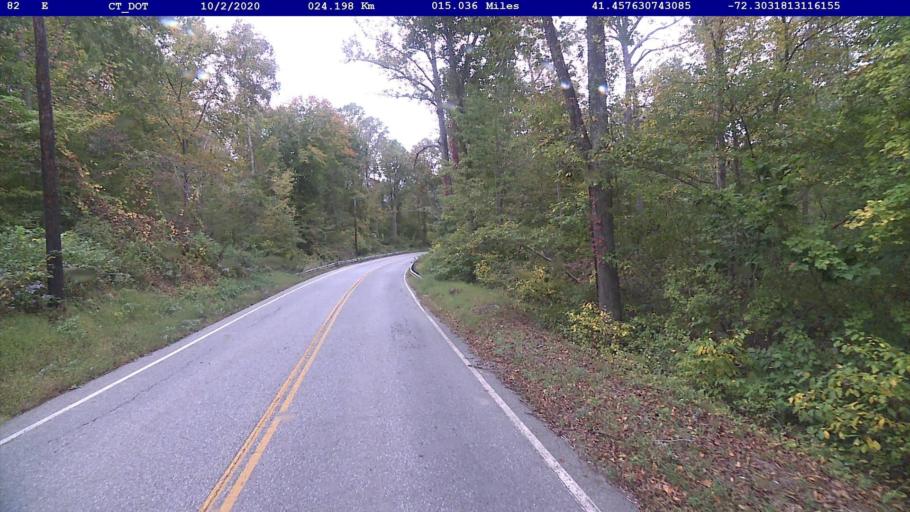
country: US
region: Connecticut
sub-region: New London County
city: Colchester
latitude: 41.4576
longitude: -72.3031
